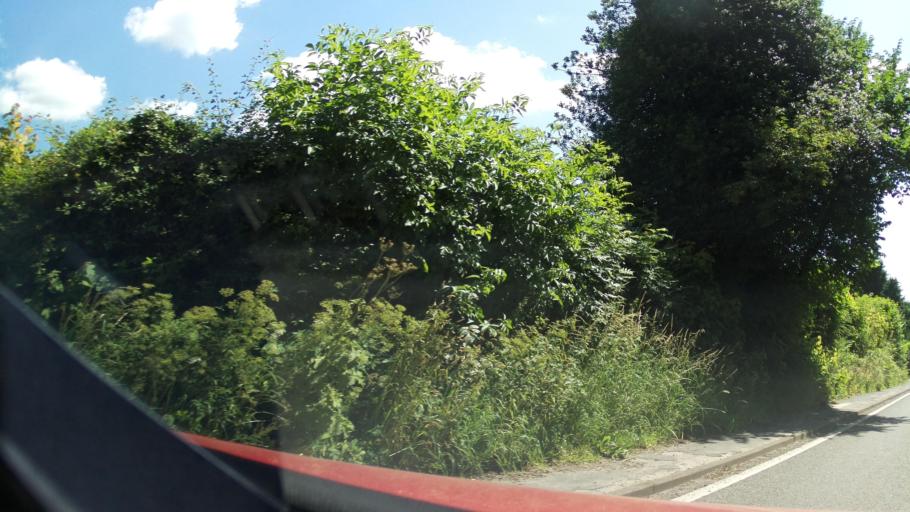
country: GB
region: England
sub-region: Derbyshire
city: Ashbourne
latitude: 53.0499
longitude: -1.7409
